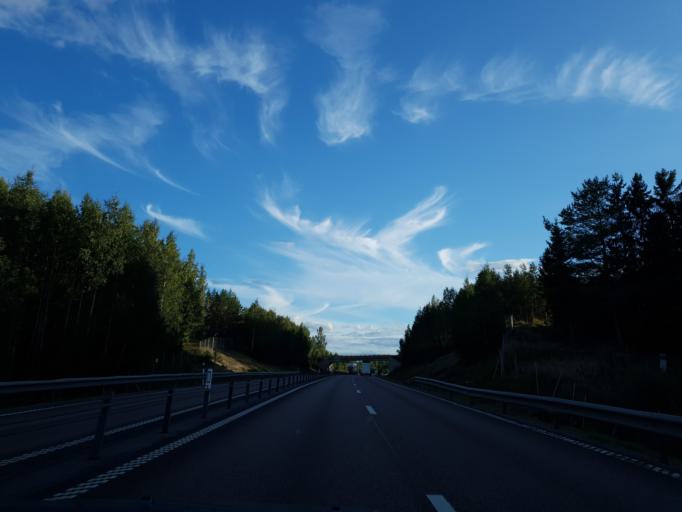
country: SE
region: Gaevleborg
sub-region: Hudiksvalls Kommun
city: Hudiksvall
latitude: 61.7617
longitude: 17.0934
